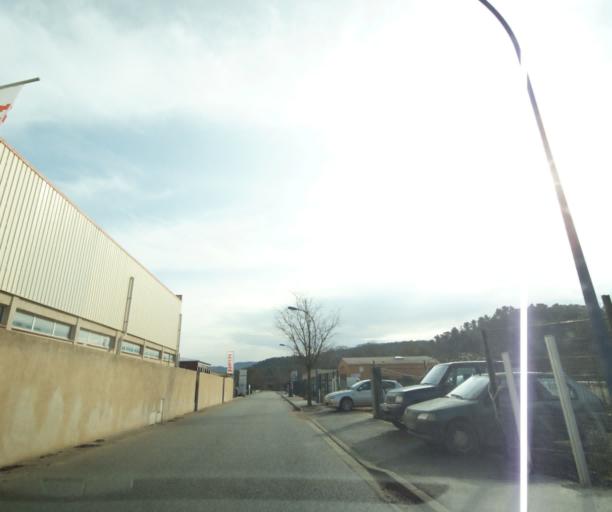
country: FR
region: Provence-Alpes-Cote d'Azur
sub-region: Departement du Var
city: Tourves
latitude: 43.4051
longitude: 5.9399
